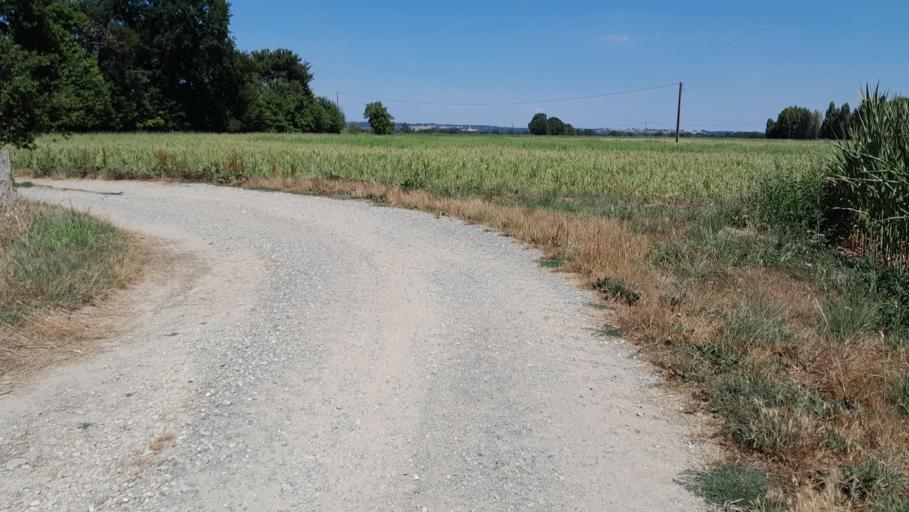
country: FR
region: Pays de la Loire
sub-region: Departement de la Mayenne
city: Ballots
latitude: 47.9647
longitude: -1.0595
